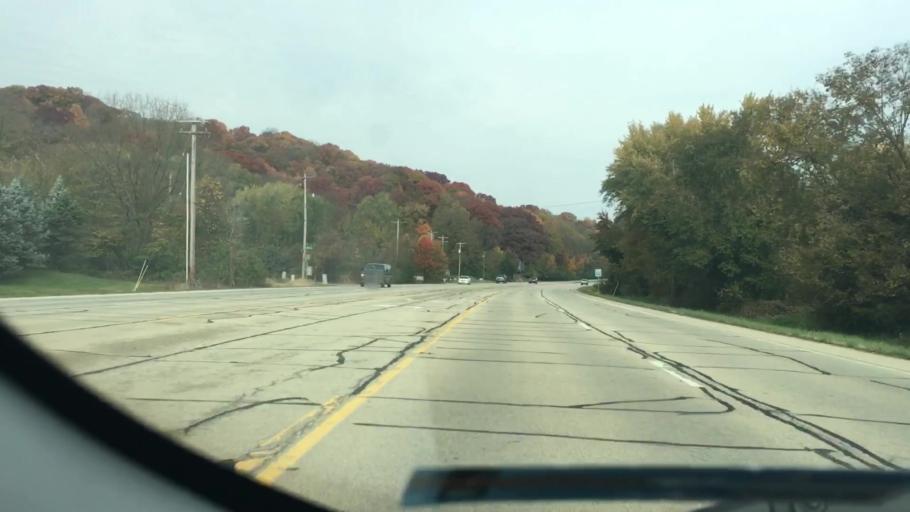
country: US
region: Illinois
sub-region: Peoria County
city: Peoria Heights
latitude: 40.7747
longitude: -89.5752
